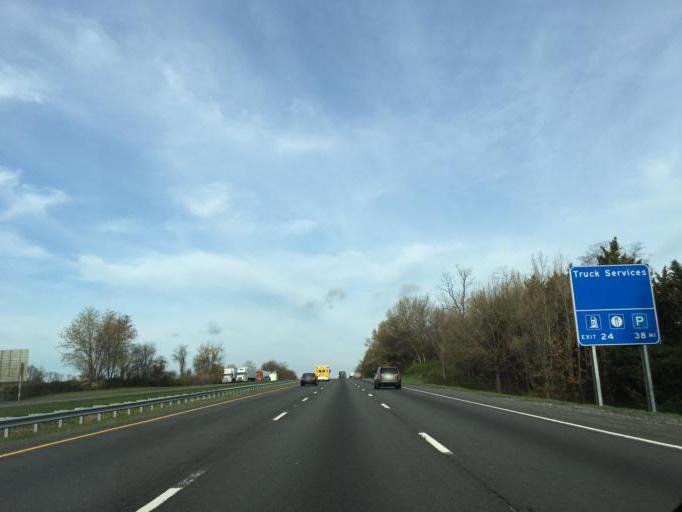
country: US
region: Maryland
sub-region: Frederick County
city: Spring Ridge
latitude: 39.3836
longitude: -77.2842
